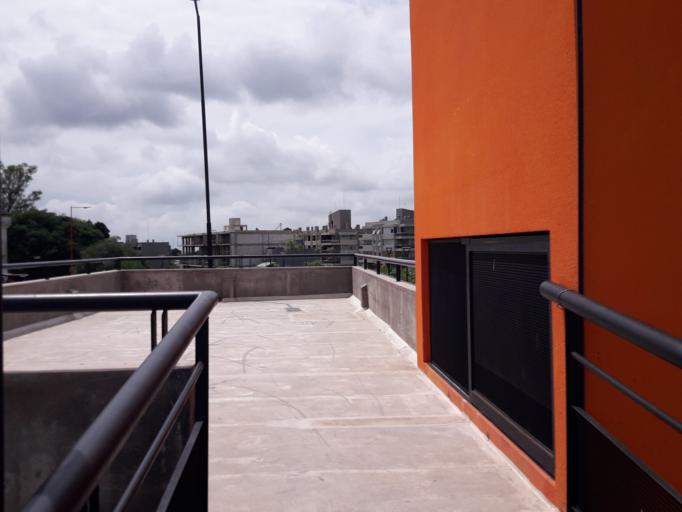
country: AR
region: Jujuy
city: San Salvador de Jujuy
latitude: -24.1830
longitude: -65.3292
